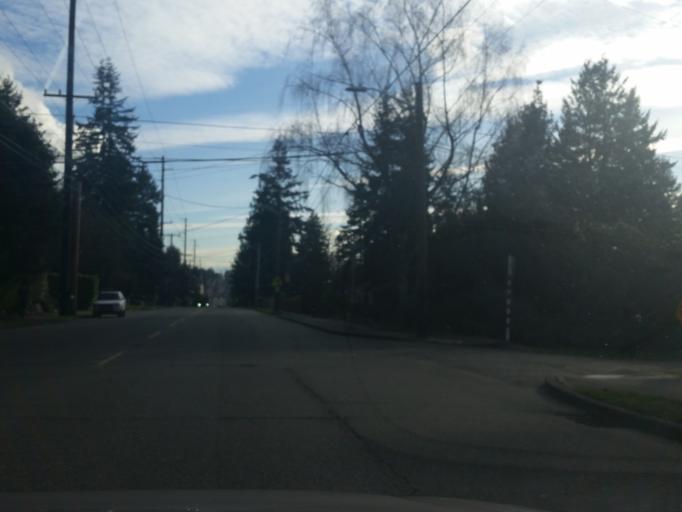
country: US
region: Washington
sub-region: King County
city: Shoreline
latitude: 47.7161
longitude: -122.3236
